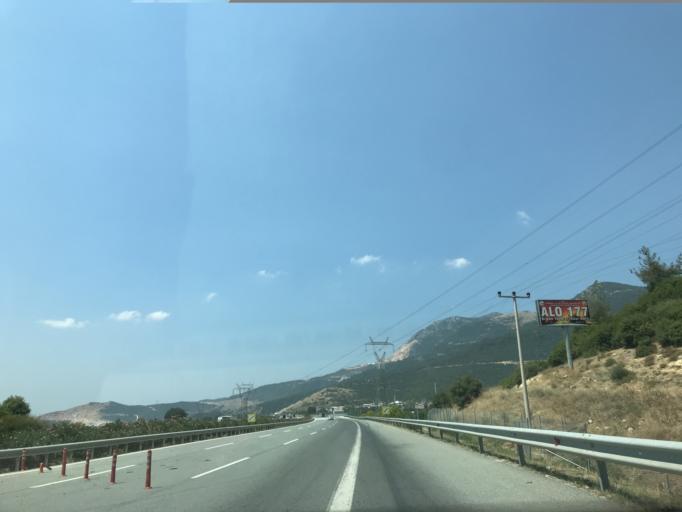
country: TR
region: Bursa
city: Kestel
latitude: 40.2419
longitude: 29.2586
